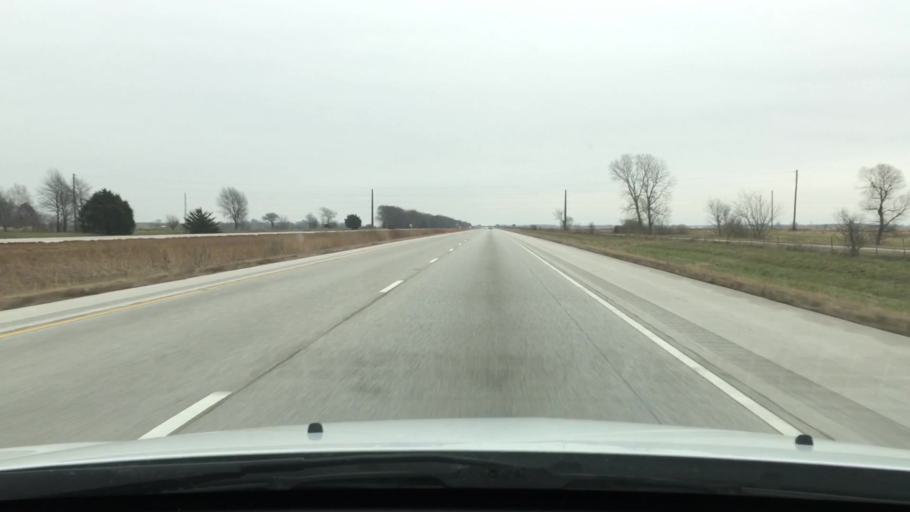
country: US
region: Illinois
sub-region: Scott County
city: Winchester
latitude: 39.6801
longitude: -90.3791
